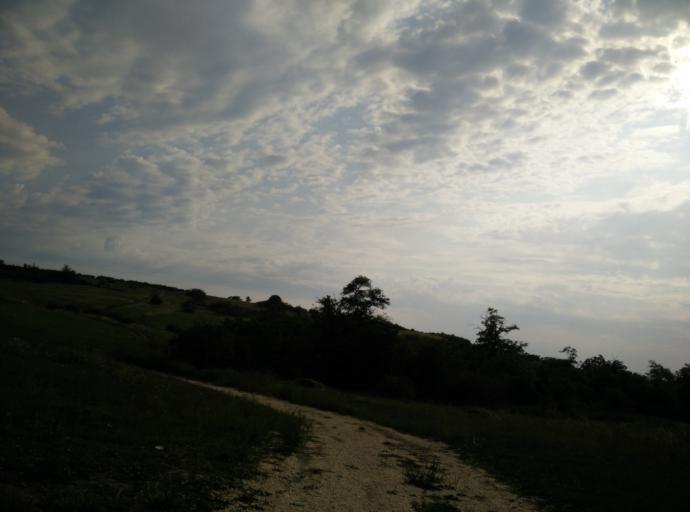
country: HU
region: Pest
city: Paty
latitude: 47.5024
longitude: 18.8430
